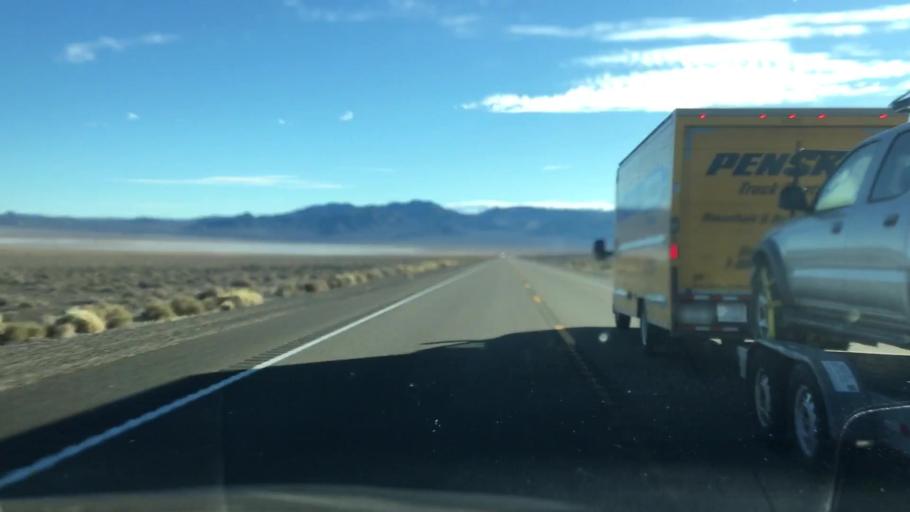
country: US
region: Nevada
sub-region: Mineral County
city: Hawthorne
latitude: 38.3244
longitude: -118.1028
